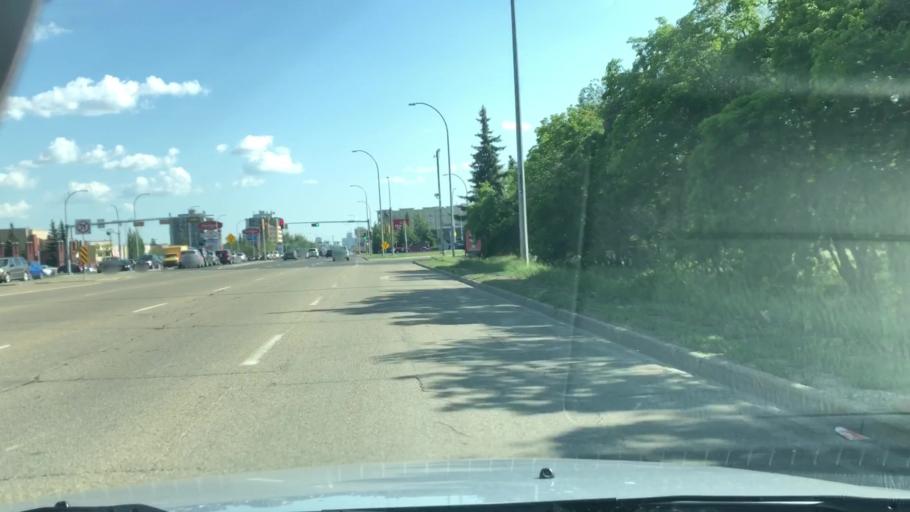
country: CA
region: Alberta
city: Edmonton
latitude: 53.6007
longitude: -113.4923
